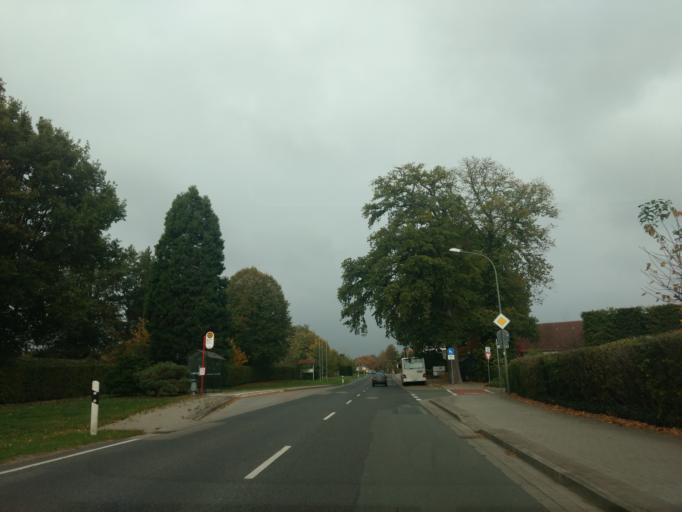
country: DE
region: Lower Saxony
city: Bad Iburg
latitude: 52.1473
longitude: 8.0506
